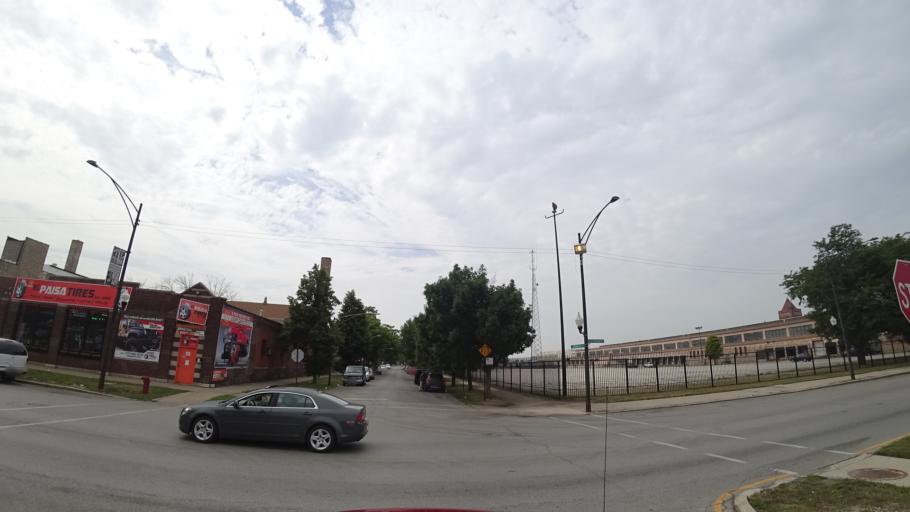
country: US
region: Illinois
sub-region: Cook County
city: Cicero
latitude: 41.8514
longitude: -87.7357
